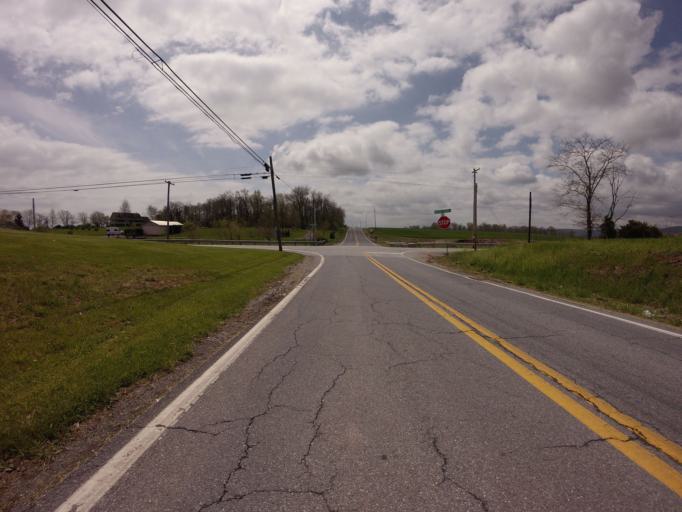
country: US
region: Maryland
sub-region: Frederick County
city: Emmitsburg
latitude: 39.6612
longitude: -77.3379
